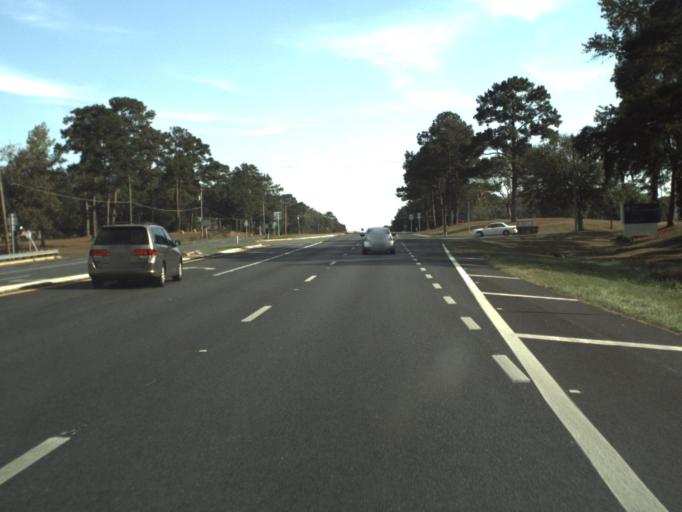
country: US
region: Florida
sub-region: Gadsden County
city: Quincy
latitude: 30.5711
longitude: -84.5498
